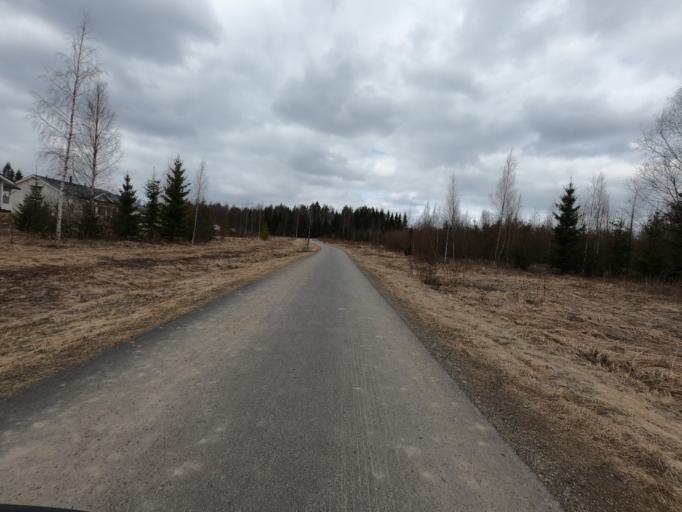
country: FI
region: North Karelia
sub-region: Joensuu
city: Joensuu
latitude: 62.5680
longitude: 29.8165
